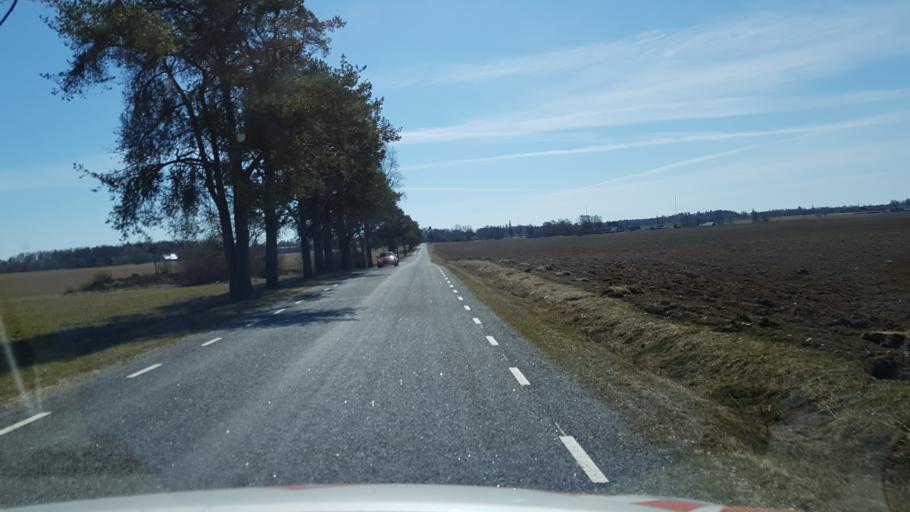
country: EE
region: Laeaene-Virumaa
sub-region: Vinni vald
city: Vinni
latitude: 59.1077
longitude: 26.5251
